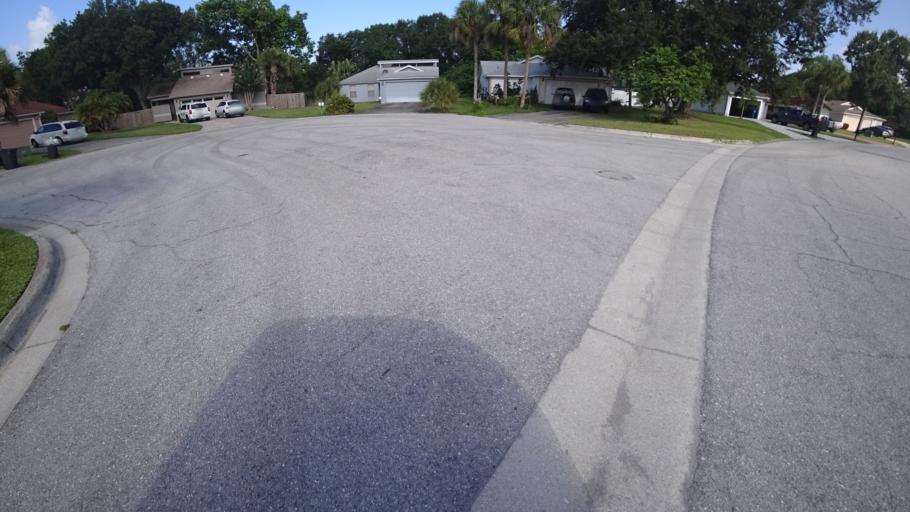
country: US
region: Florida
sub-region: Sarasota County
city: North Sarasota
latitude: 27.3931
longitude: -82.5029
